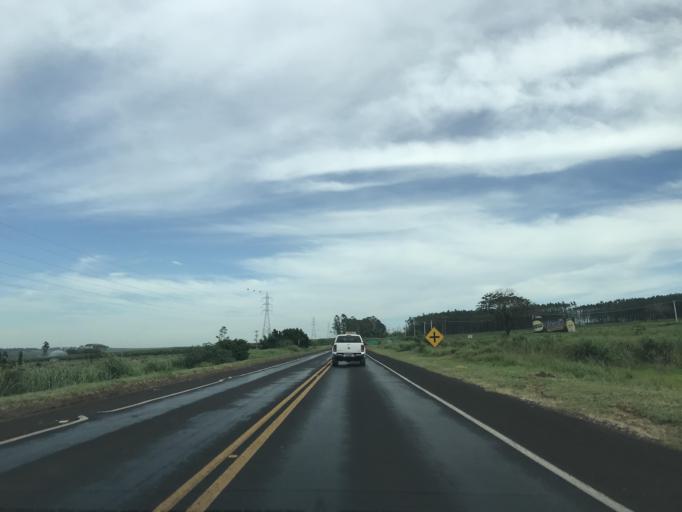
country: BR
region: Parana
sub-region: Paranavai
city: Nova Aurora
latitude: -22.9924
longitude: -52.5923
